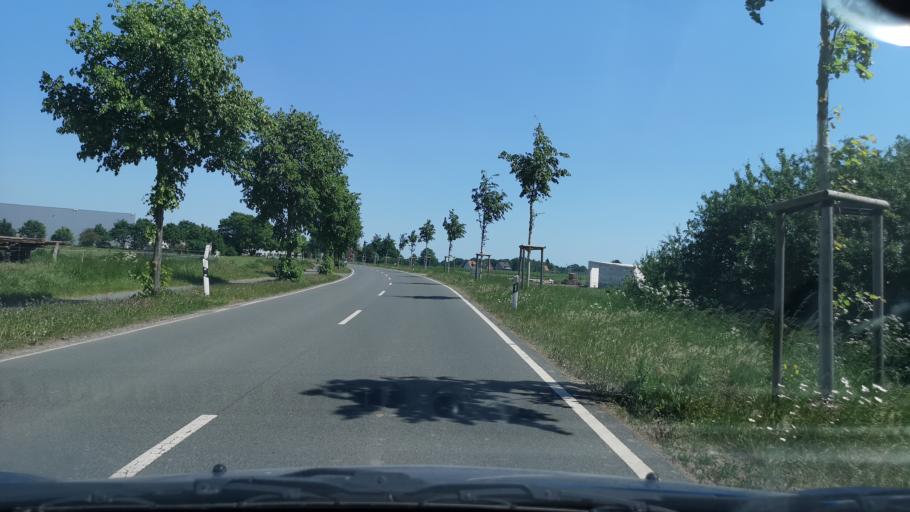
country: DE
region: Lower Saxony
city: Garbsen
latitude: 52.4515
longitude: 9.5627
